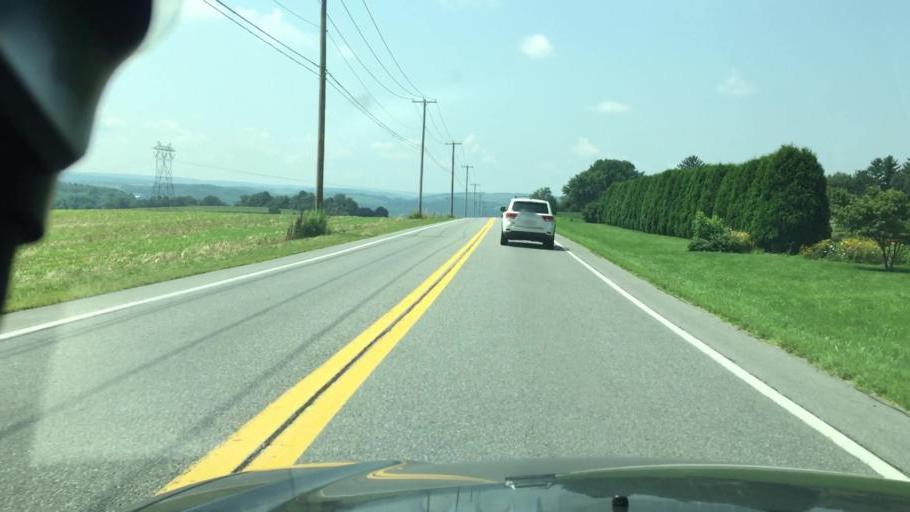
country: US
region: Pennsylvania
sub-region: Columbia County
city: Catawissa
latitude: 40.9236
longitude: -76.4645
